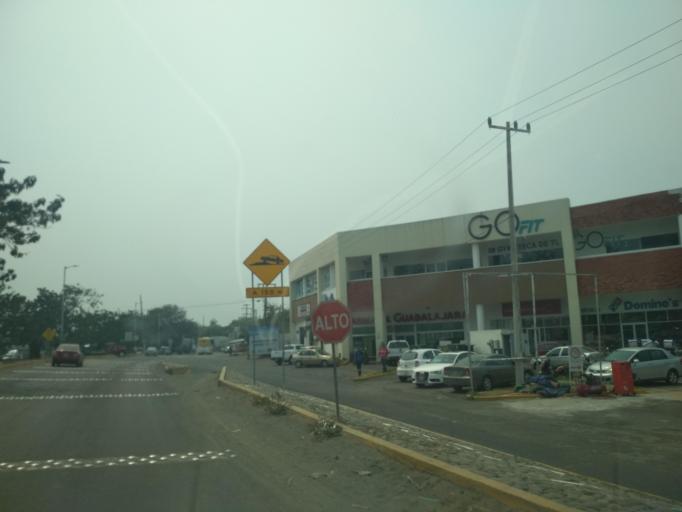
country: MX
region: Veracruz
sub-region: Veracruz
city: Lomas de Rio Medio Cuatro
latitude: 19.1708
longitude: -96.2291
